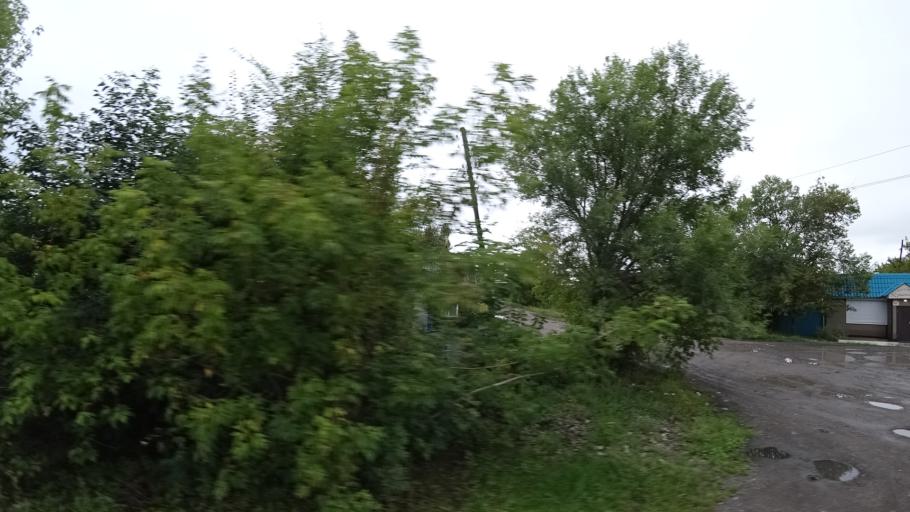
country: RU
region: Primorskiy
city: Chernigovka
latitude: 44.3341
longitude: 132.5313
